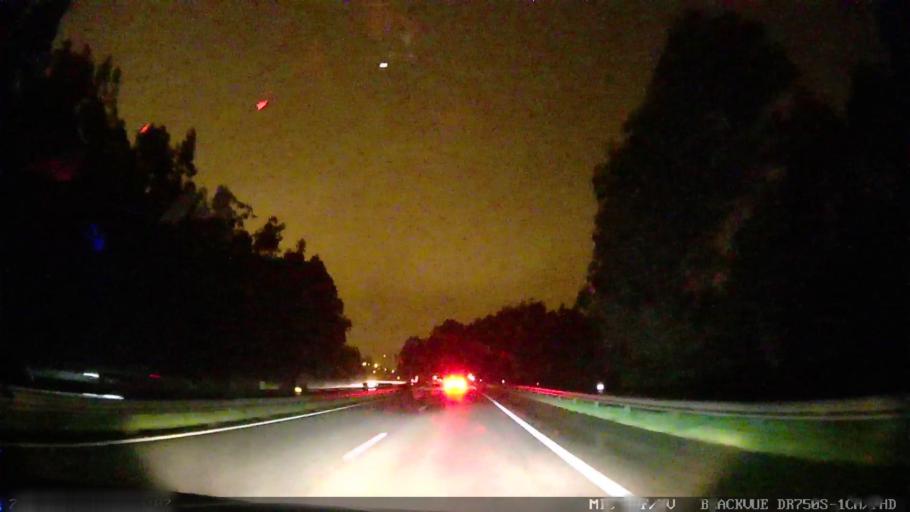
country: PT
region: Porto
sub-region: Penafiel
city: Penafiel
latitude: 41.2185
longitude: -8.2689
